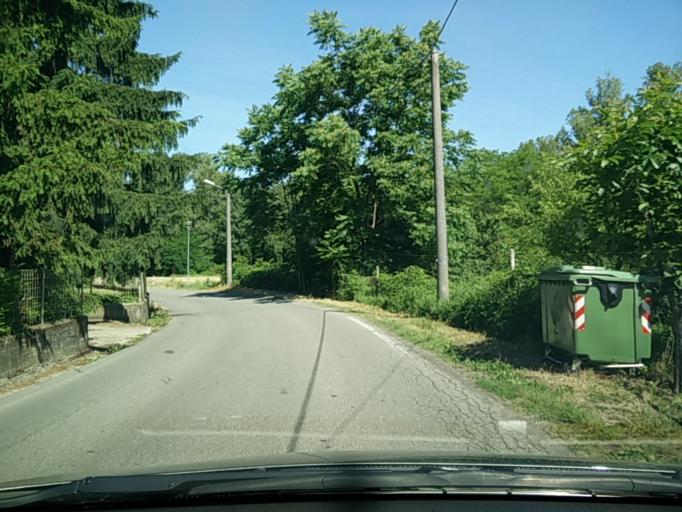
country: IT
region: Lombardy
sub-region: Provincia di Pavia
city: Salice Terme
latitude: 44.9066
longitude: 9.0409
